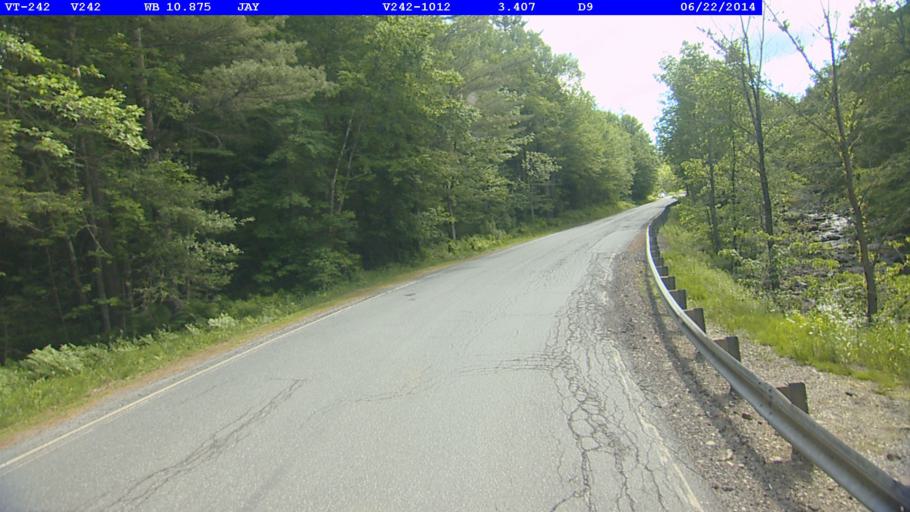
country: CA
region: Quebec
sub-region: Monteregie
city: Sutton
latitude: 44.9446
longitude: -72.4494
